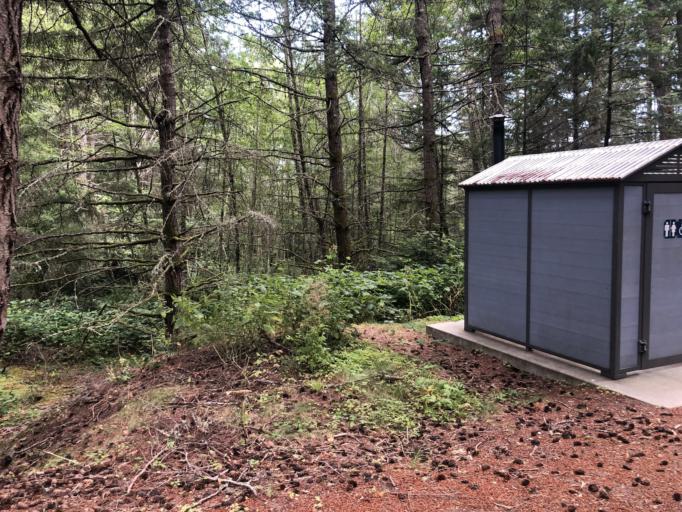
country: CA
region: British Columbia
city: Metchosin
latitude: 48.3887
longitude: -123.5209
